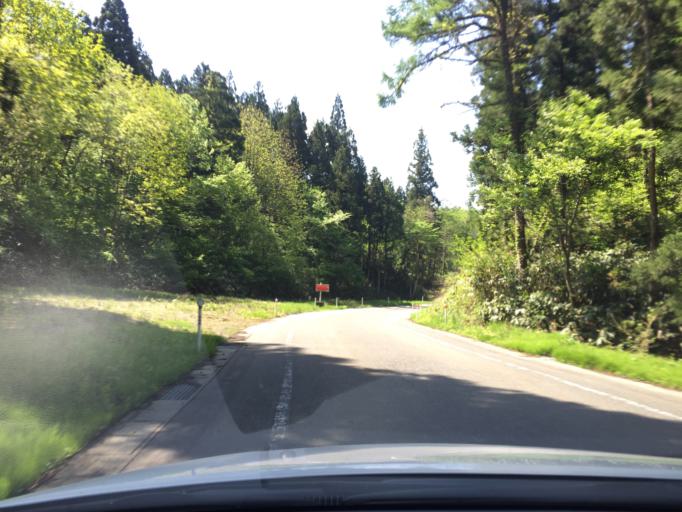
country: JP
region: Niigata
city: Kamo
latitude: 37.5739
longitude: 139.0857
